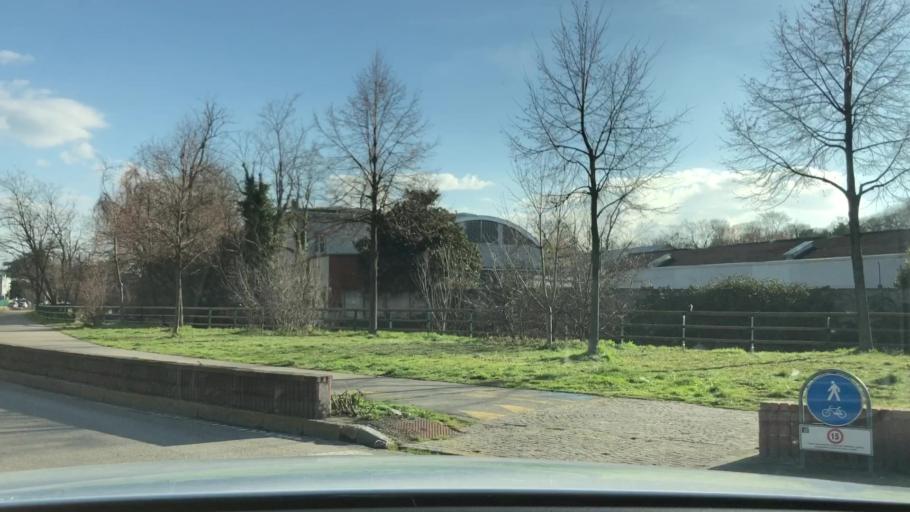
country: IT
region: Lombardy
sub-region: Citta metropolitana di Milano
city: Bresso
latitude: 45.5423
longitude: 9.1814
